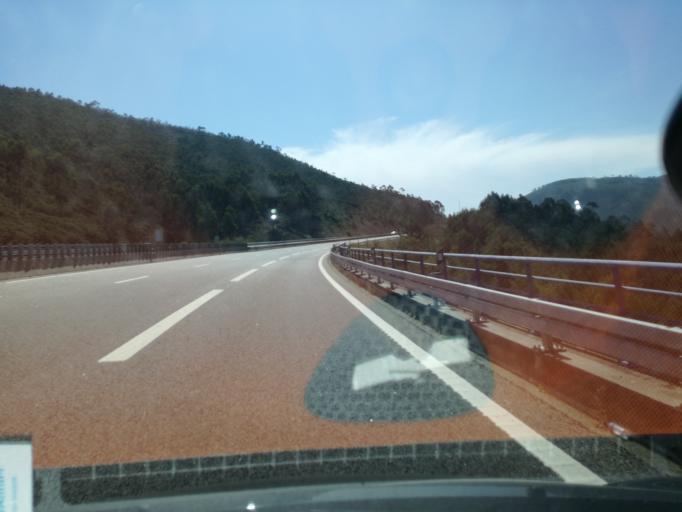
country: PT
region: Viana do Castelo
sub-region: Vila Nova de Cerveira
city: Vila Nova de Cerveira
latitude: 41.8744
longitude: -8.7847
